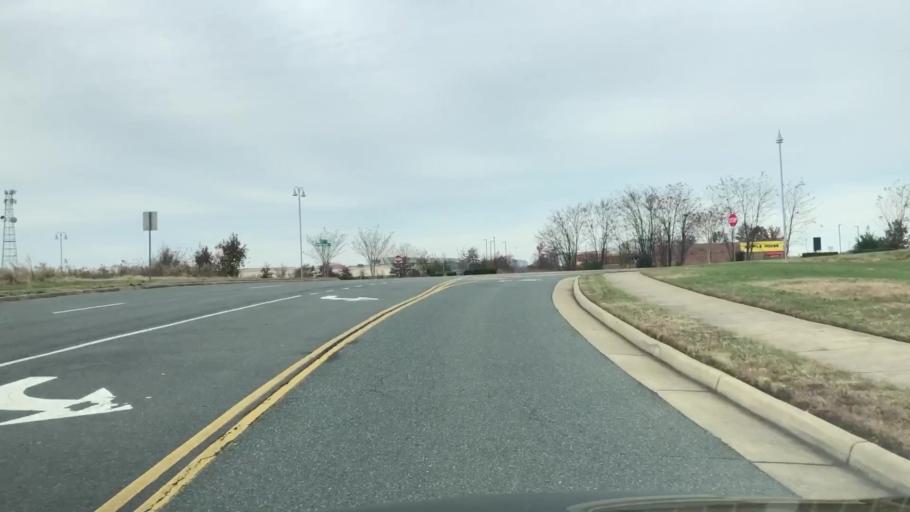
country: US
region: Virginia
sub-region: Stafford County
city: Falmouth
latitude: 38.3579
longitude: -77.5184
